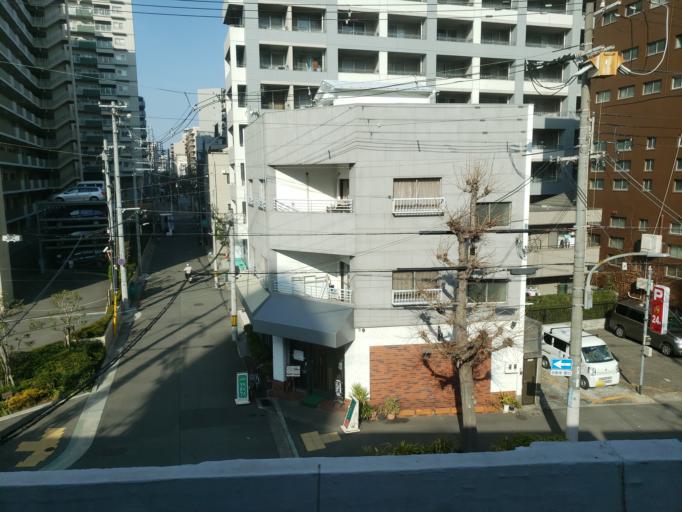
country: JP
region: Hyogo
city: Kobe
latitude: 34.6760
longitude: 135.1769
